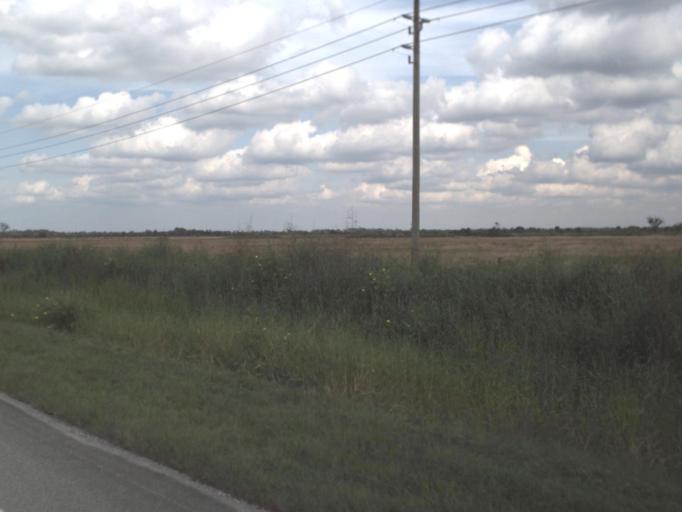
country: US
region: Florida
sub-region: Okeechobee County
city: Cypress Quarters
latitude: 27.4661
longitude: -80.8086
